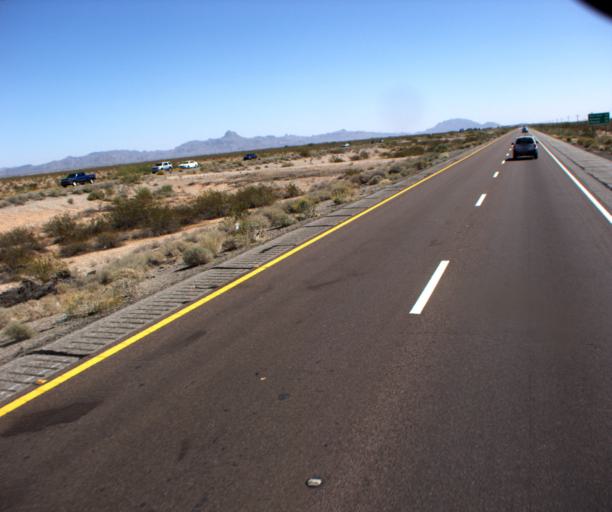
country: US
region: Arizona
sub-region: La Paz County
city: Salome
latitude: 33.5655
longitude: -113.3318
